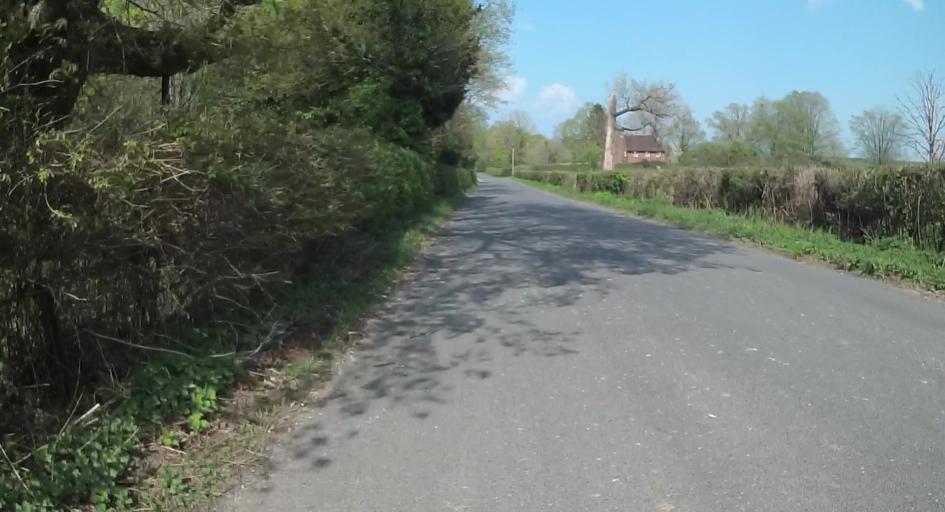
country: GB
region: England
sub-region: Hampshire
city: Basingstoke
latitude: 51.3078
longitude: -1.0863
